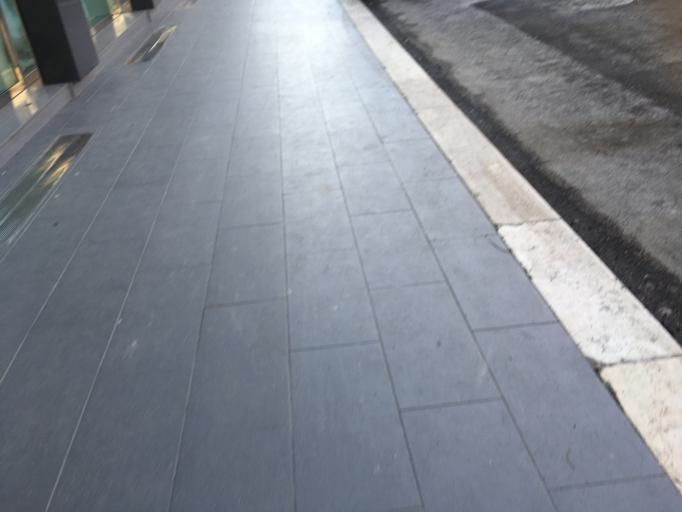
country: IT
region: Apulia
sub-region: Provincia di Barletta - Andria - Trani
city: Andria
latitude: 41.2217
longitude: 16.3032
